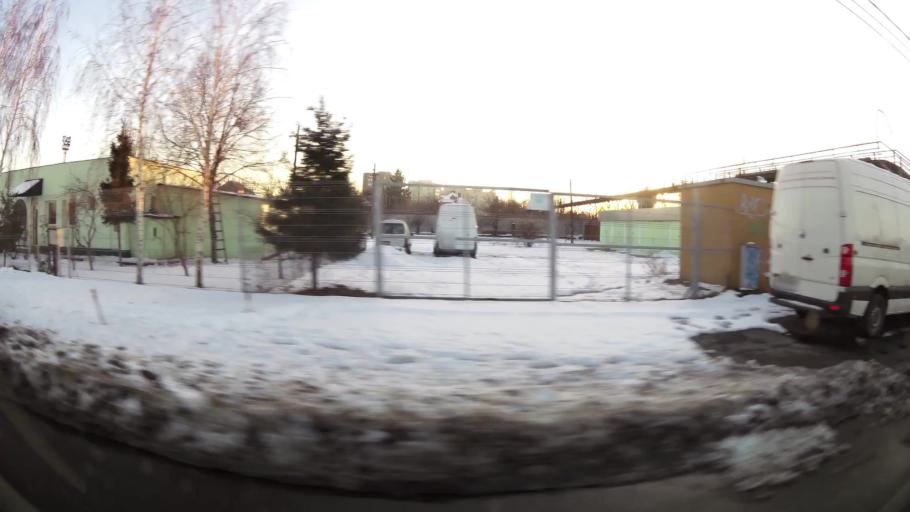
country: RO
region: Ilfov
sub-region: Comuna Fundeni-Dobroesti
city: Fundeni
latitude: 44.4502
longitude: 26.1404
